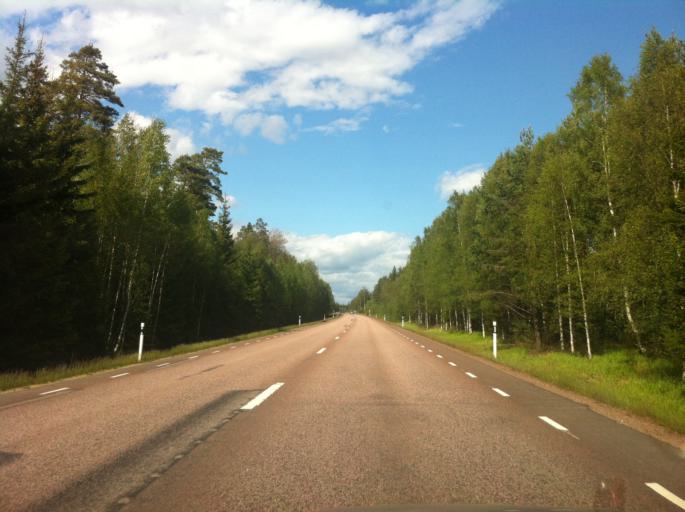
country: SE
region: Vaermland
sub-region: Kristinehamns Kommun
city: Kristinehamn
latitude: 59.3727
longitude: 14.1689
